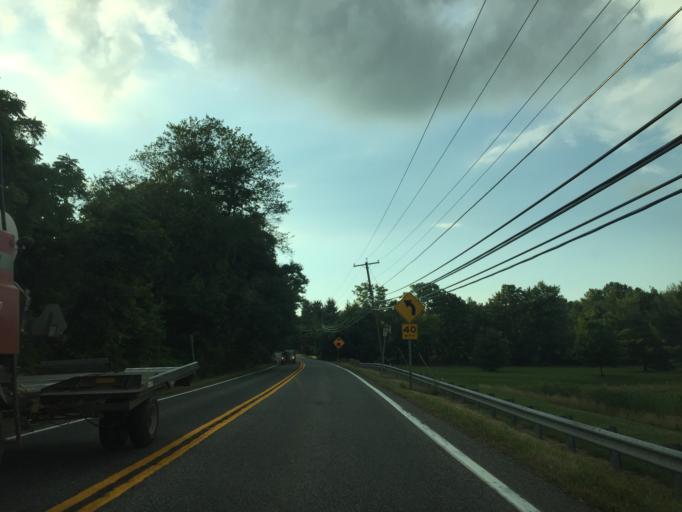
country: US
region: Maryland
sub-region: Harford County
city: Jarrettsville
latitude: 39.5885
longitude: -76.5069
